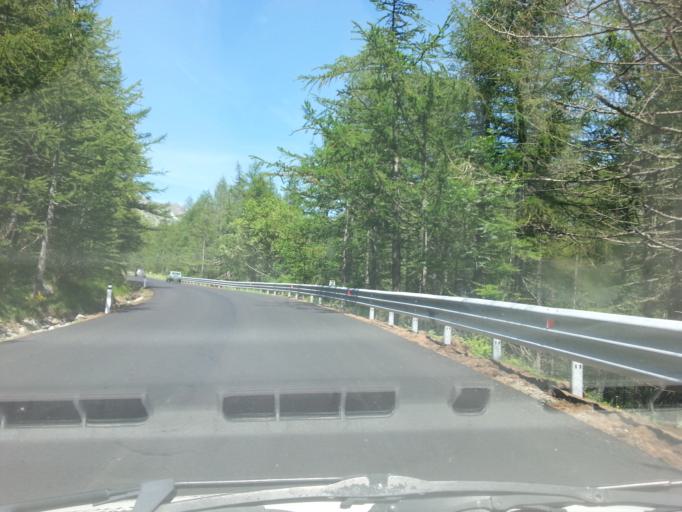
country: IT
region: Piedmont
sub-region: Provincia di Torino
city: Moncenisio
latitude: 45.1990
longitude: 6.9776
